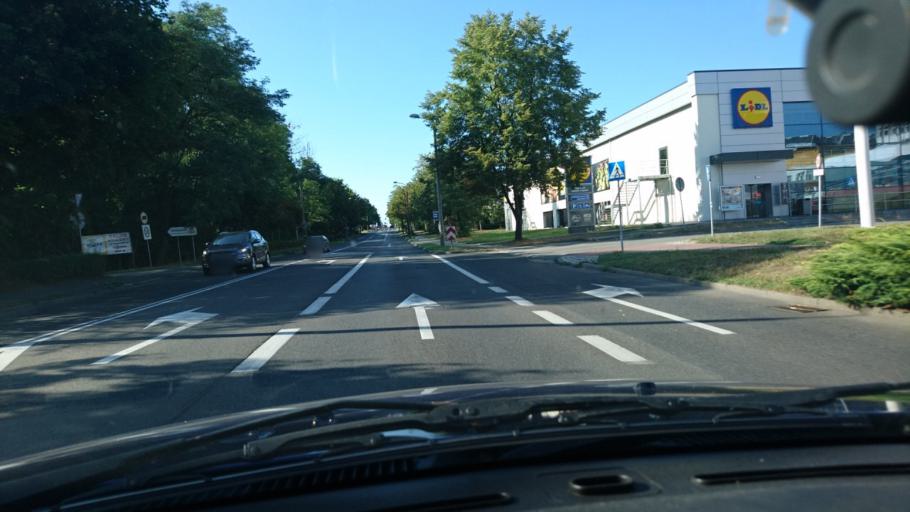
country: PL
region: Silesian Voivodeship
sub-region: Gliwice
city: Gliwice
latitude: 50.3211
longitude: 18.6637
